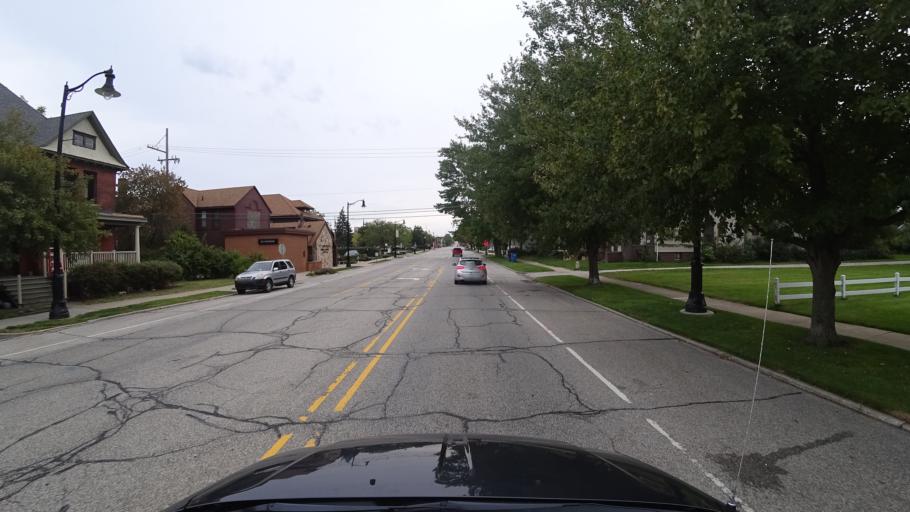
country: US
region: Indiana
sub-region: LaPorte County
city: Michigan City
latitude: 41.7177
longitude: -86.9037
